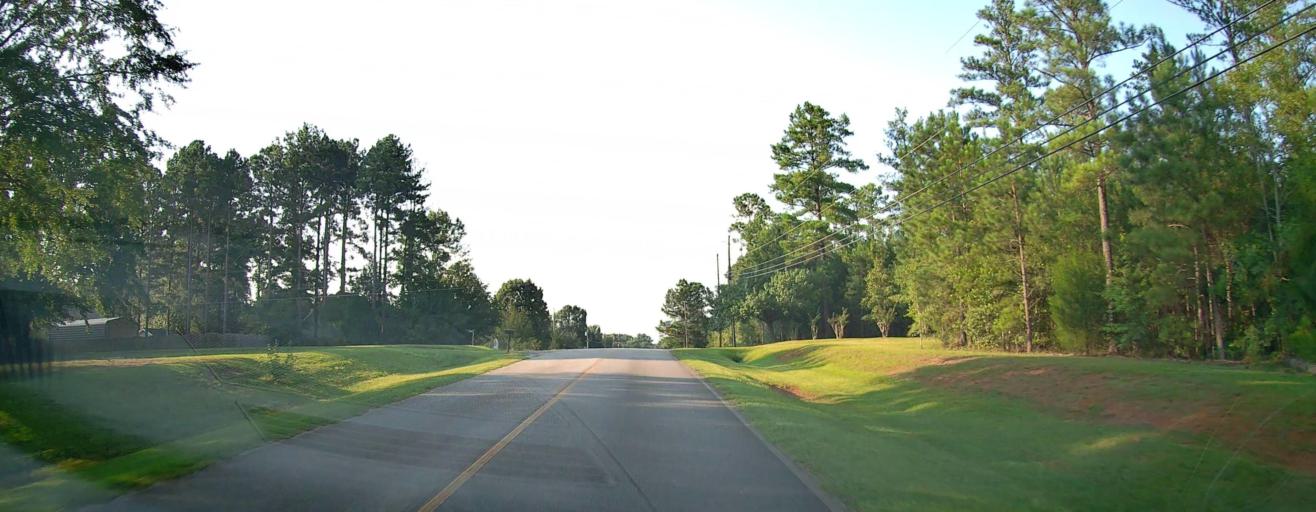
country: US
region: Georgia
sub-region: Peach County
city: Byron
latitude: 32.7241
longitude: -83.7467
